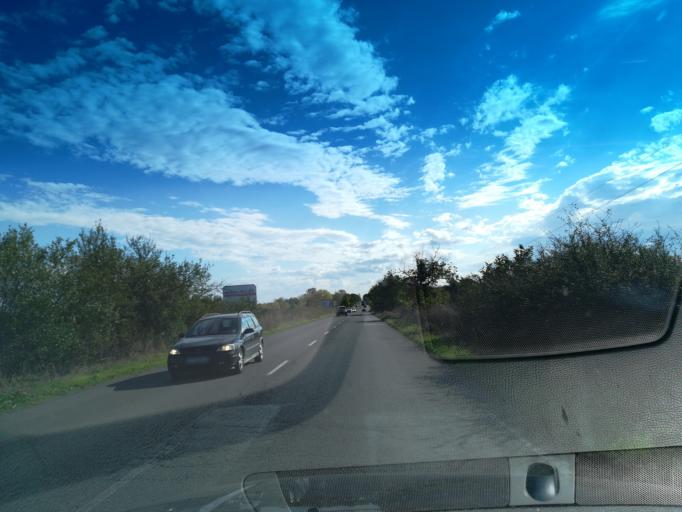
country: BG
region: Stara Zagora
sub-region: Obshtina Stara Zagora
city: Stara Zagora
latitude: 42.3637
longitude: 25.6551
